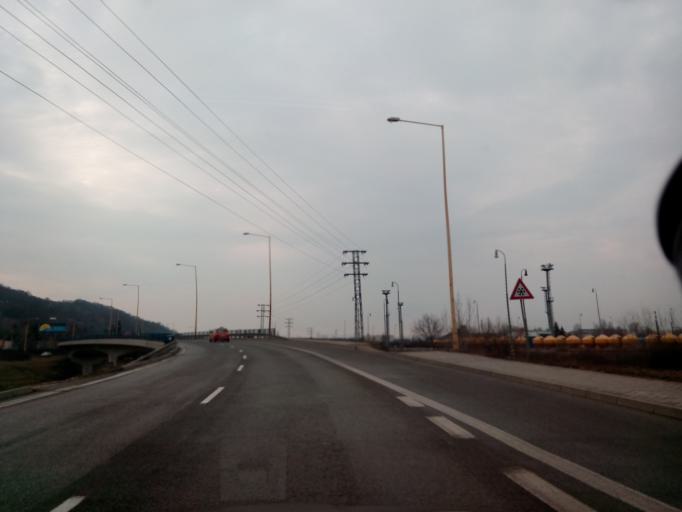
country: SK
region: Kosicky
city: Kosice
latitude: 48.7197
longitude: 21.2761
